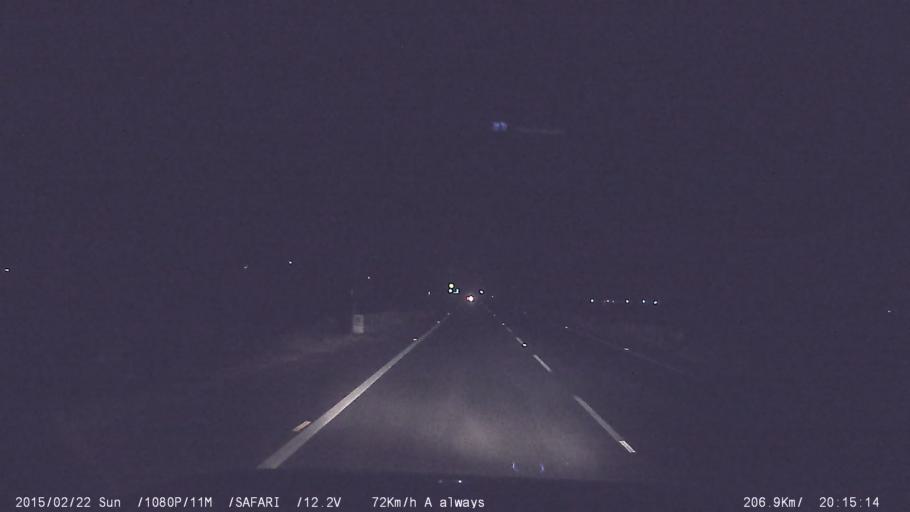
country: IN
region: Tamil Nadu
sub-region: Dindigul
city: Nilakottai
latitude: 10.2595
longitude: 77.8394
